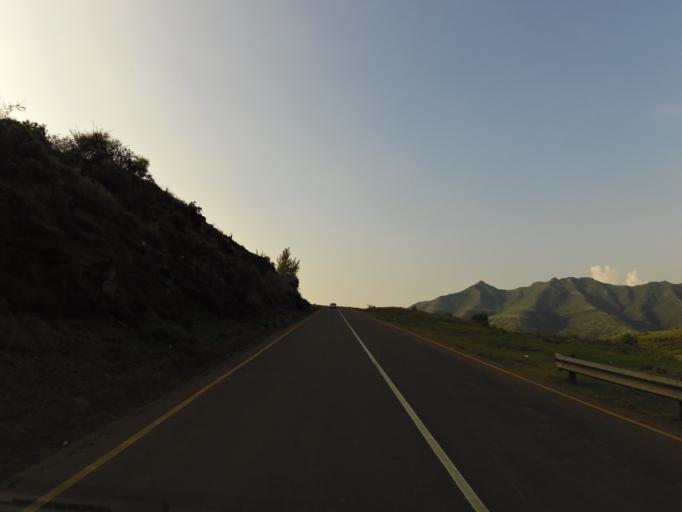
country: LS
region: Butha-Buthe
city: Butha-Buthe
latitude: -29.0369
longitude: 28.2784
